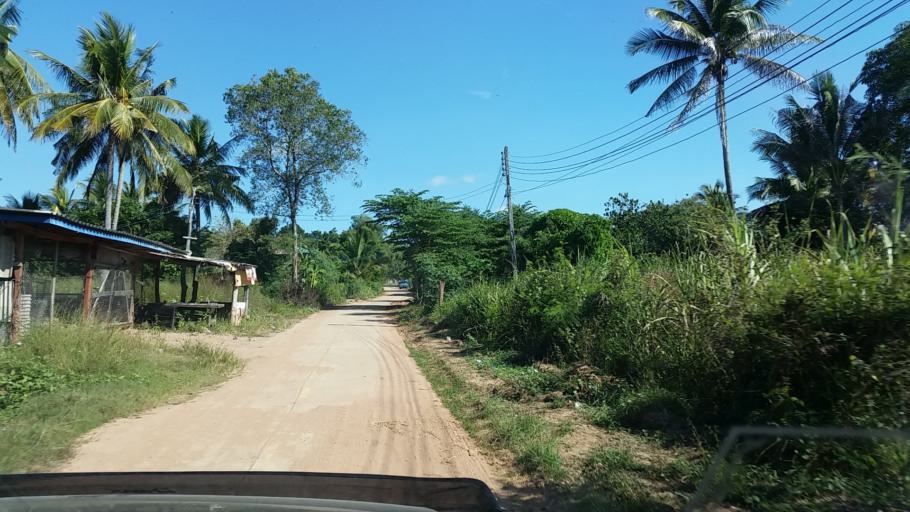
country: TH
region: Chaiyaphum
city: Thep Sathit
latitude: 15.5404
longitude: 101.4886
